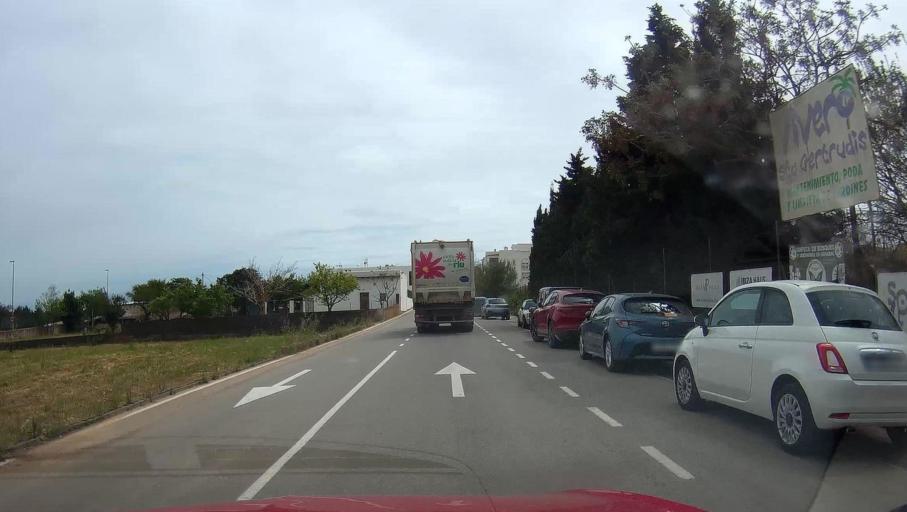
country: ES
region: Balearic Islands
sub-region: Illes Balears
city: Ibiza
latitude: 39.0015
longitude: 1.4292
